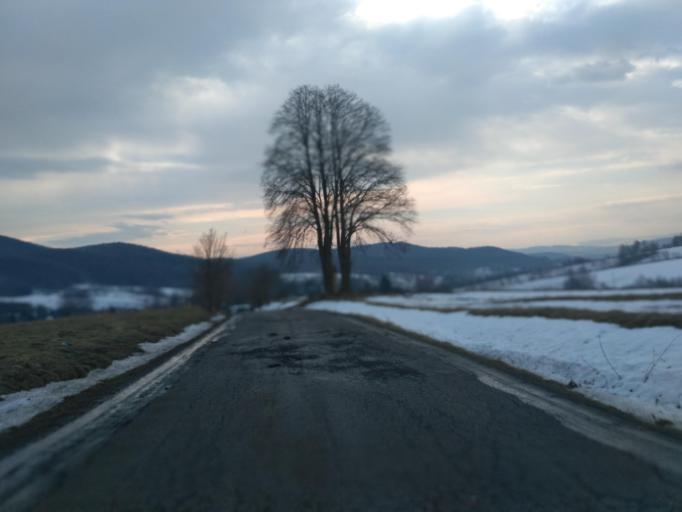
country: PL
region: Subcarpathian Voivodeship
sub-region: Powiat brzozowski
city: Dydnia
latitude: 49.6383
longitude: 22.1647
